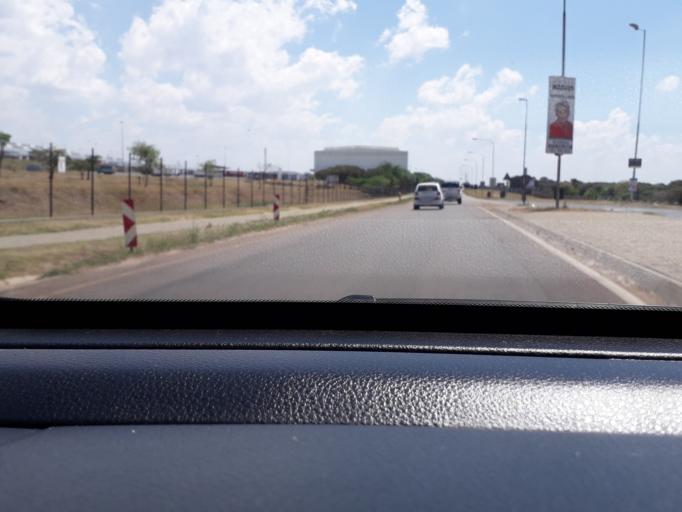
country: ZA
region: Gauteng
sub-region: City of Tshwane Metropolitan Municipality
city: Centurion
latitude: -25.9120
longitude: 28.1749
